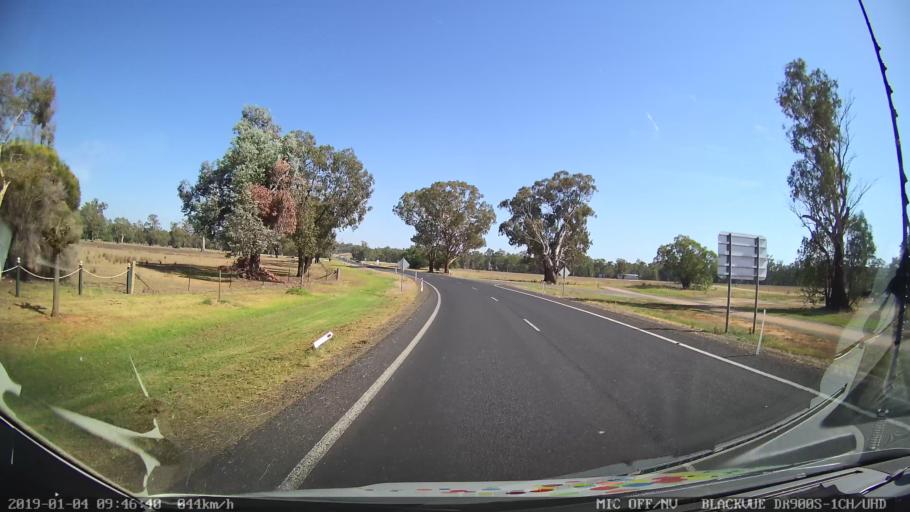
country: AU
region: New South Wales
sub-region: Cabonne
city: Canowindra
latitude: -33.6134
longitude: 148.4354
